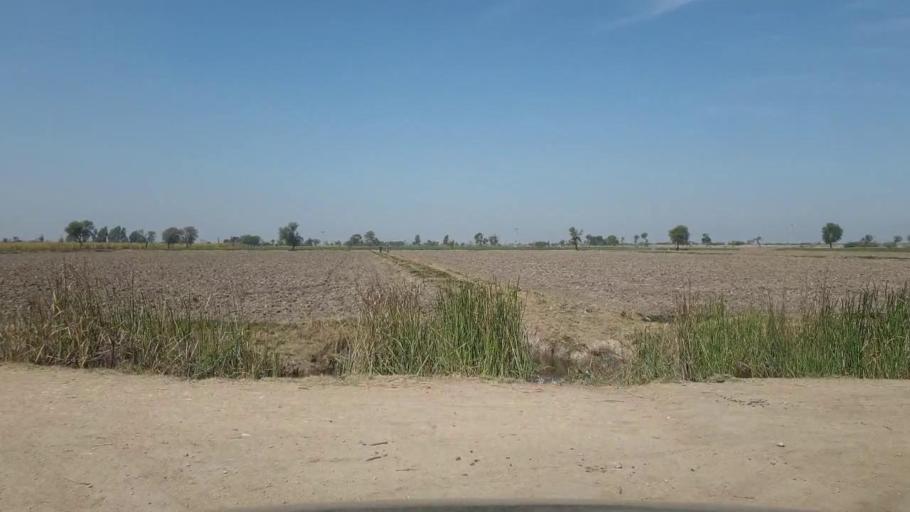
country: PK
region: Sindh
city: Mirpur Khas
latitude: 25.4447
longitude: 69.1633
